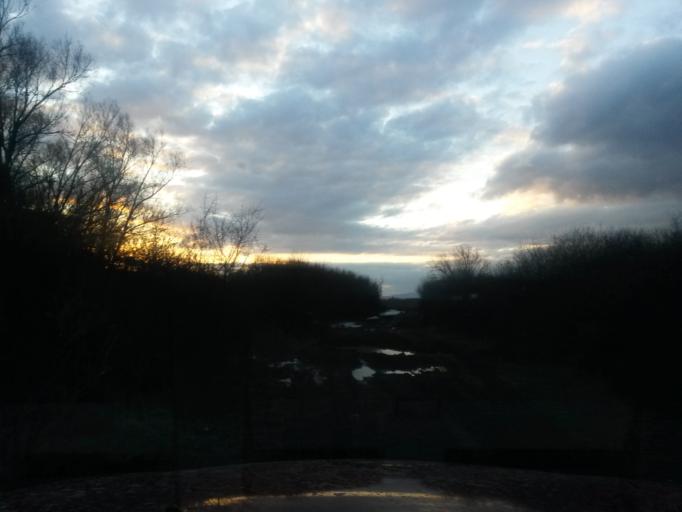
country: SK
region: Kosicky
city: Sobrance
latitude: 48.7023
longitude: 22.0640
